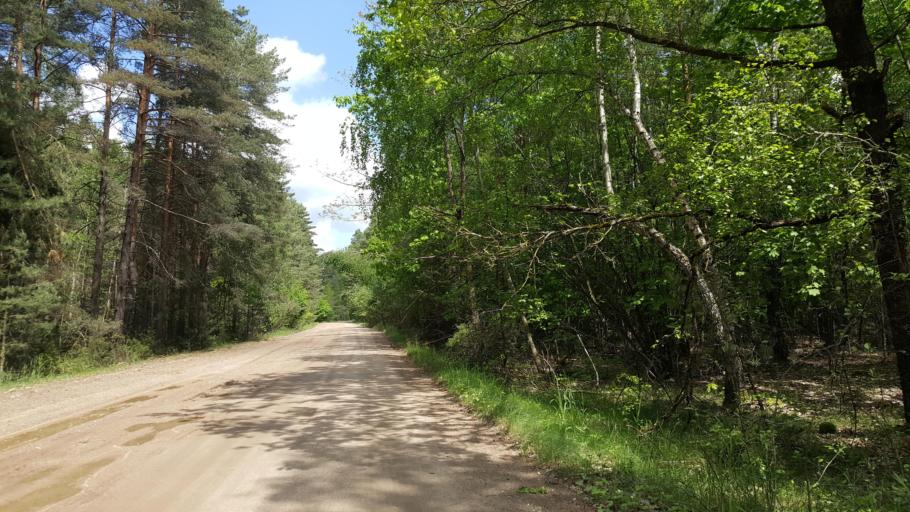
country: BY
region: Brest
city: Kamyanyets
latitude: 52.4698
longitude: 23.9680
